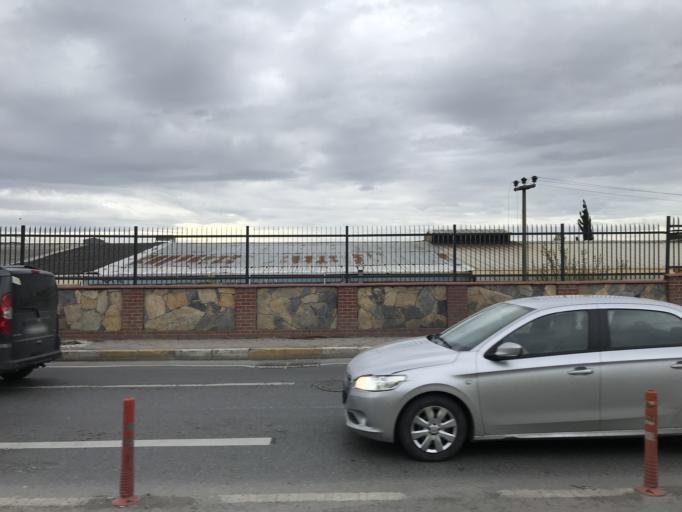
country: TR
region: Istanbul
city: Umraniye
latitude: 41.0068
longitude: 29.1616
